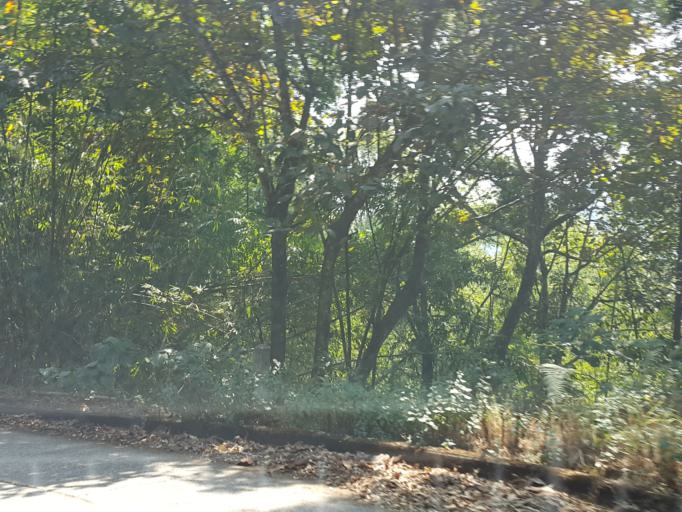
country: TH
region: Chiang Mai
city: Mae On
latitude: 18.8474
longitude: 99.3744
